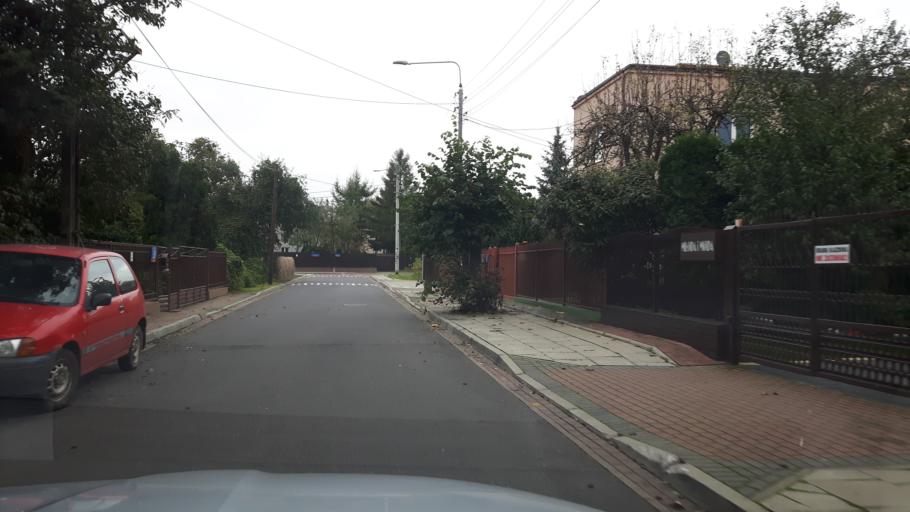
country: PL
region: Masovian Voivodeship
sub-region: Warszawa
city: Praga Poludnie
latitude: 52.2428
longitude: 21.1193
